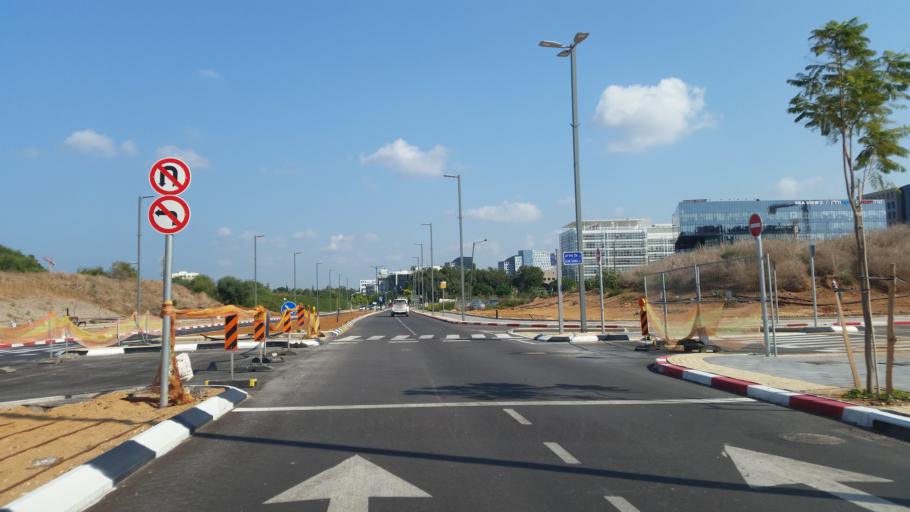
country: IL
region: Tel Aviv
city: Herzliya Pituah
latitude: 32.1579
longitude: 34.8038
